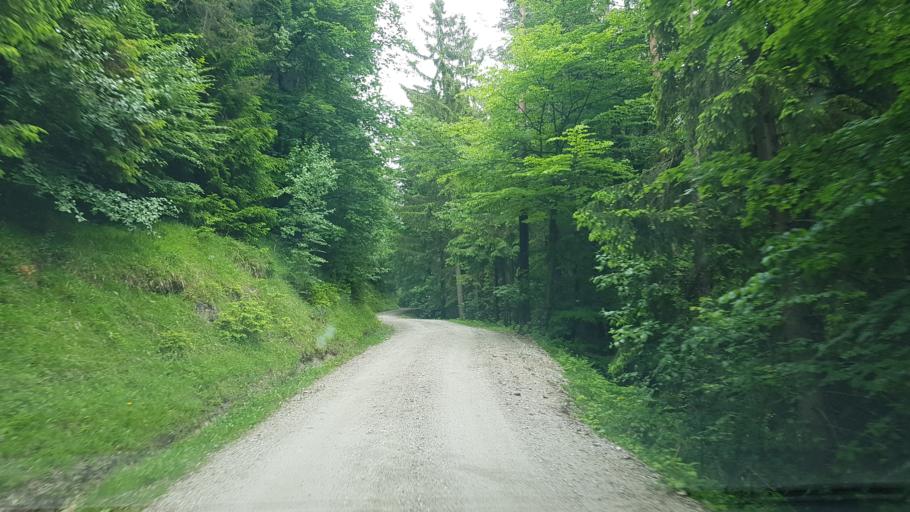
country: SI
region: Dobrna
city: Dobrna
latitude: 46.3849
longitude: 15.2164
